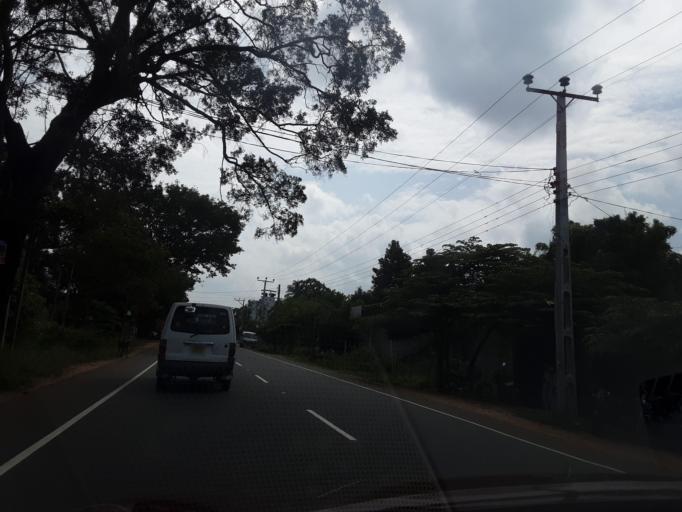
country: LK
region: North Central
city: Anuradhapura
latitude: 8.4724
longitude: 80.5127
